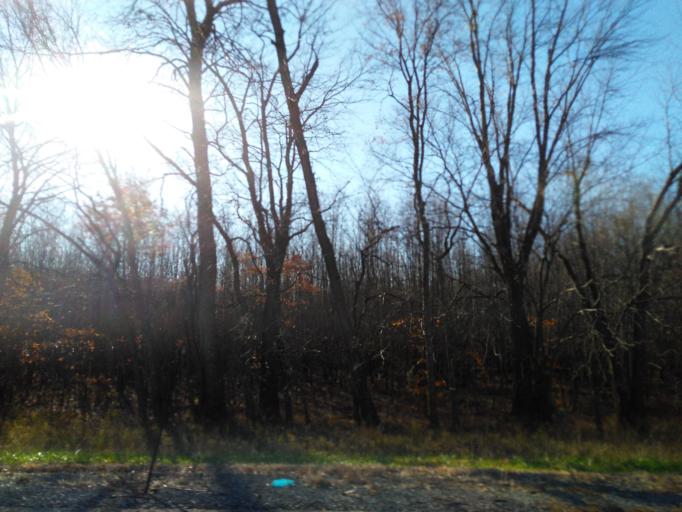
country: US
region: Illinois
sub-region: Madison County
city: Troy
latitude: 38.7613
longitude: -89.8287
